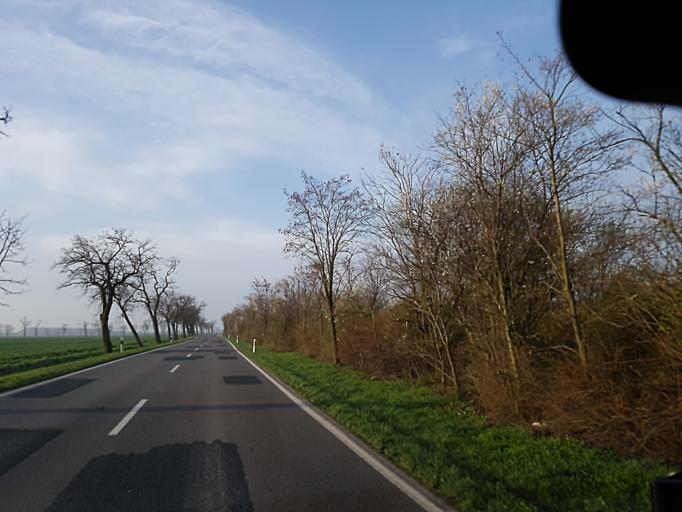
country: DE
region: Brandenburg
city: Muhlberg
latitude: 51.4399
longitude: 13.2693
